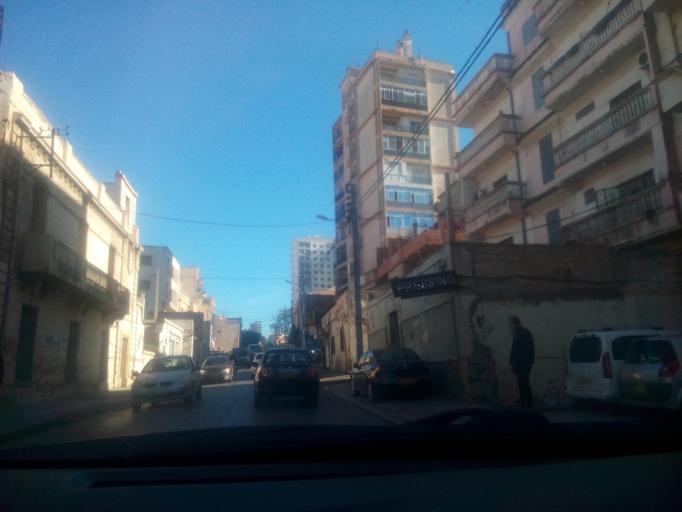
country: DZ
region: Oran
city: Oran
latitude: 35.7070
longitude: -0.6195
